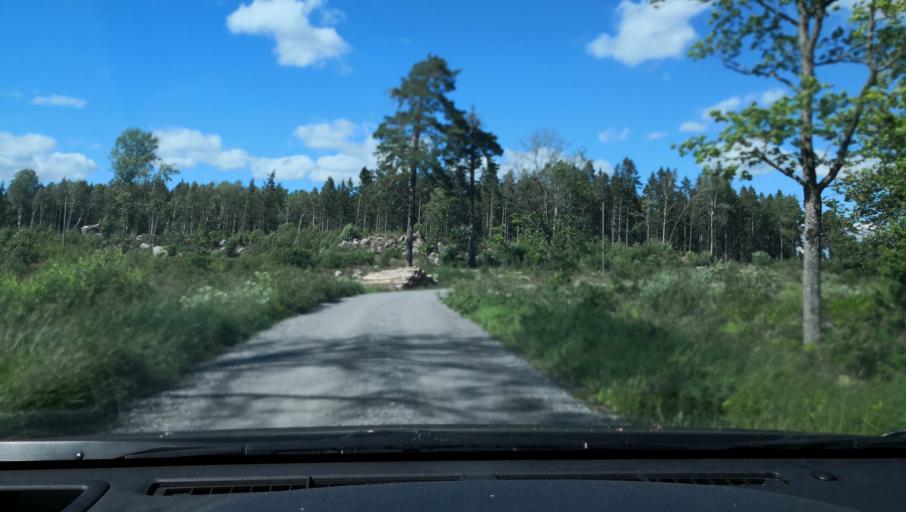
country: SE
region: Soedermanland
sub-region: Eskilstuna Kommun
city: Hallbybrunn
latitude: 59.3021
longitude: 16.3605
